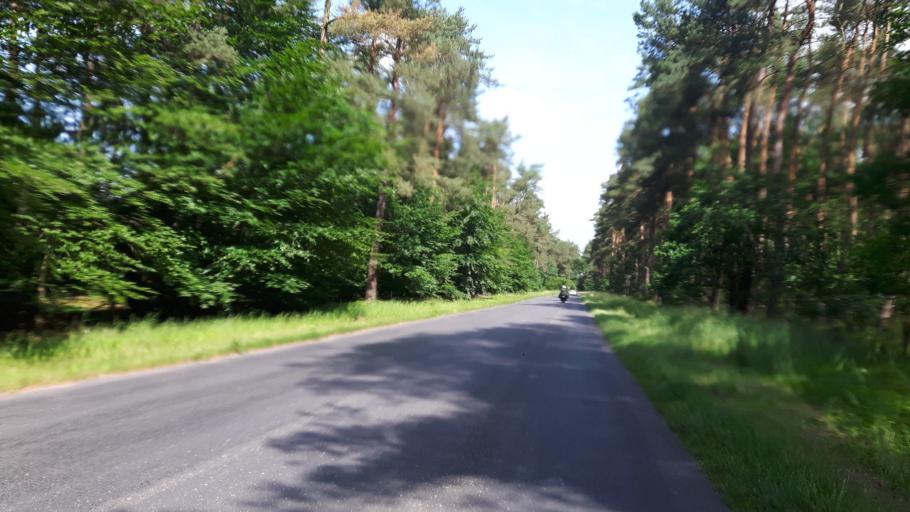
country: PL
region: West Pomeranian Voivodeship
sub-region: Powiat goleniowski
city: Goleniow
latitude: 53.5155
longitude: 14.7877
